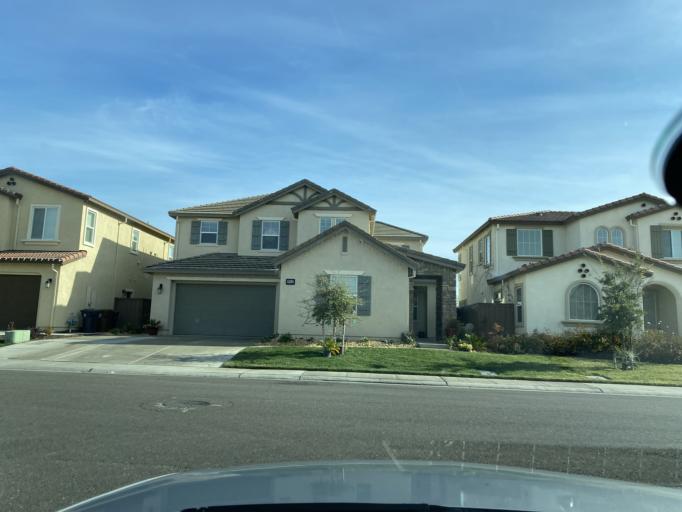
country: US
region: California
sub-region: Sacramento County
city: Elk Grove
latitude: 38.4035
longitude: -121.3967
